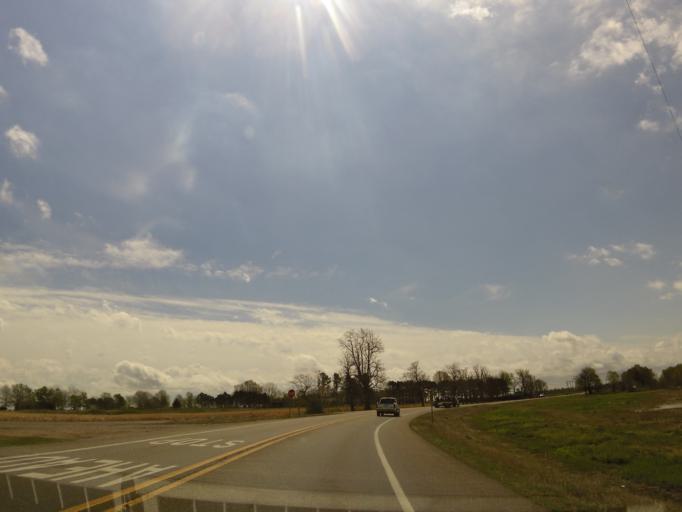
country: US
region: Arkansas
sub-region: Clay County
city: Corning
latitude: 36.3991
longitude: -90.5155
